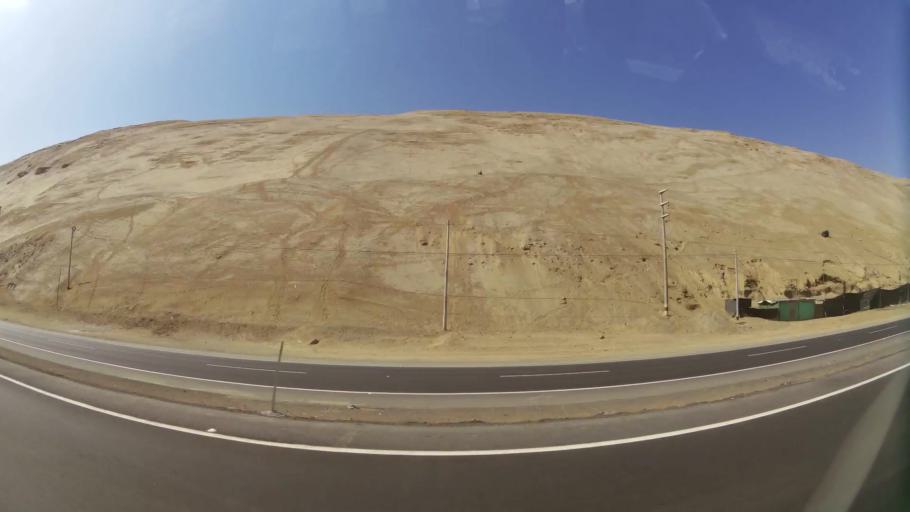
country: PE
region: Ica
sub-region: Provincia de Chincha
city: San Pedro
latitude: -13.3638
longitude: -76.2151
